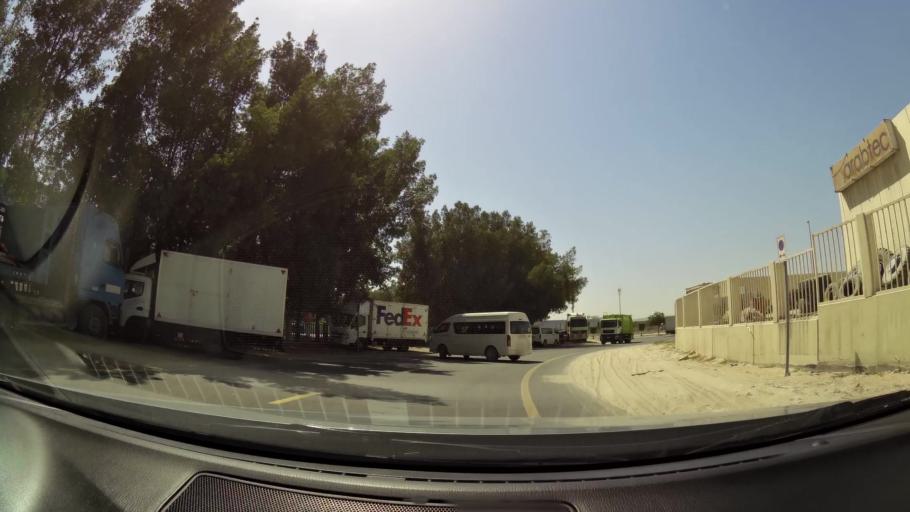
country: AE
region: Dubai
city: Dubai
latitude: 24.9696
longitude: 55.1748
